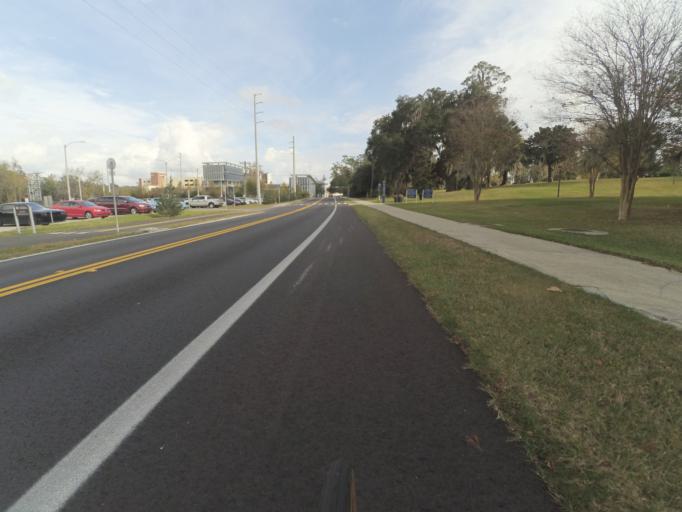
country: US
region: Florida
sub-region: Alachua County
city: Gainesville
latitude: 29.6386
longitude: -82.3519
